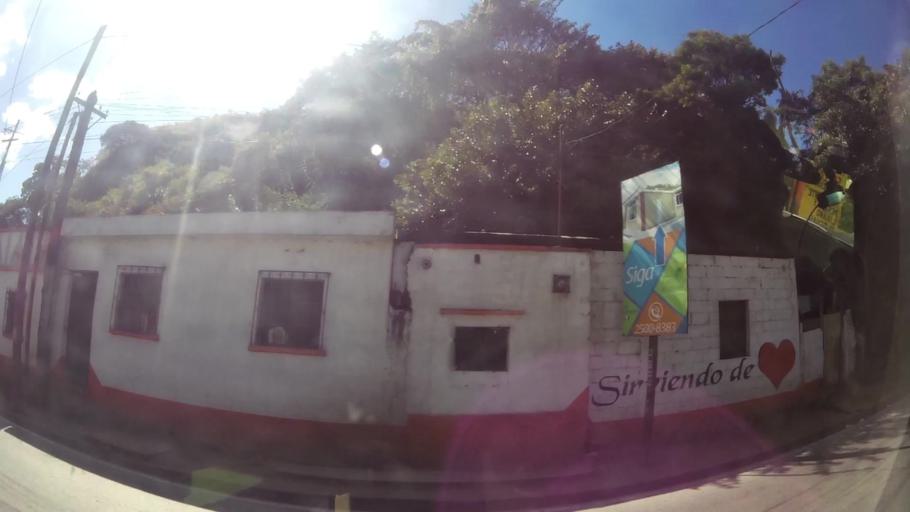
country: GT
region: Guatemala
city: Villa Canales
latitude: 14.4848
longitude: -90.5364
